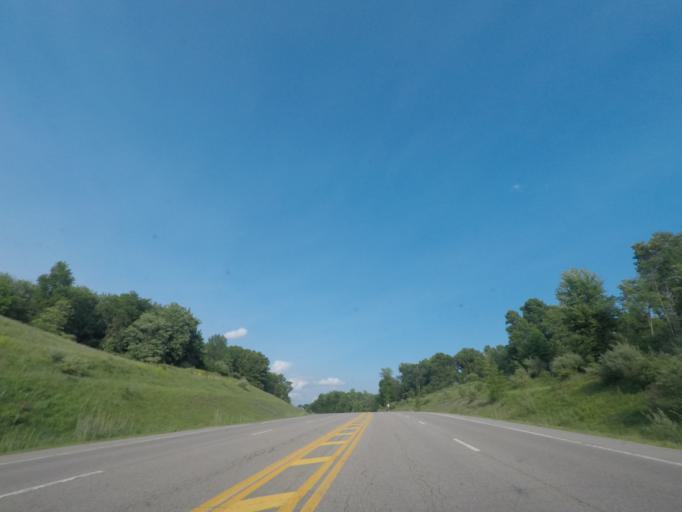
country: US
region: New York
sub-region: Orange County
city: Orange Lake
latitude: 41.4968
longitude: -74.1262
